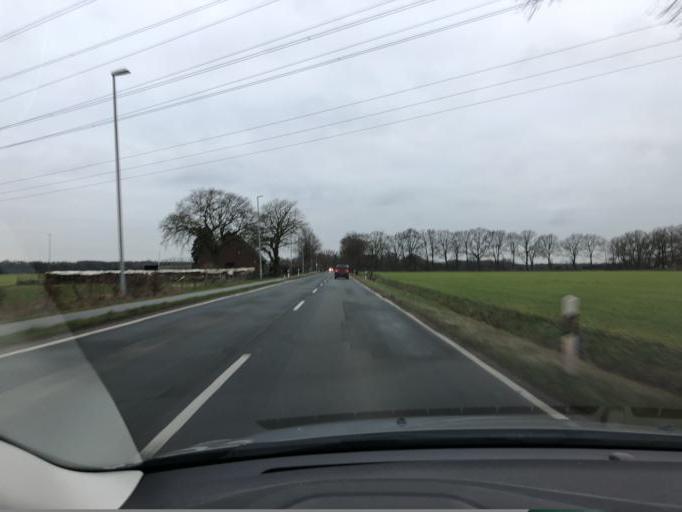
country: DE
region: Lower Saxony
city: Ganderkesee
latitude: 53.0607
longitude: 8.5691
